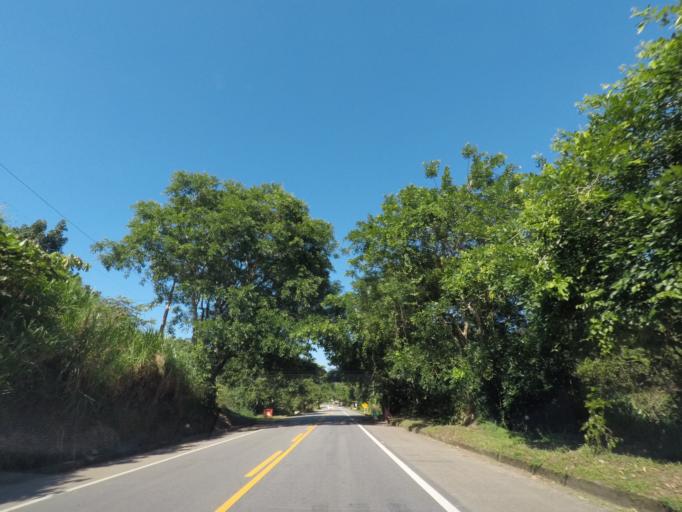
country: BR
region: Rio de Janeiro
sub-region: Parati
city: Paraty
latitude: -23.3094
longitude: -44.7125
